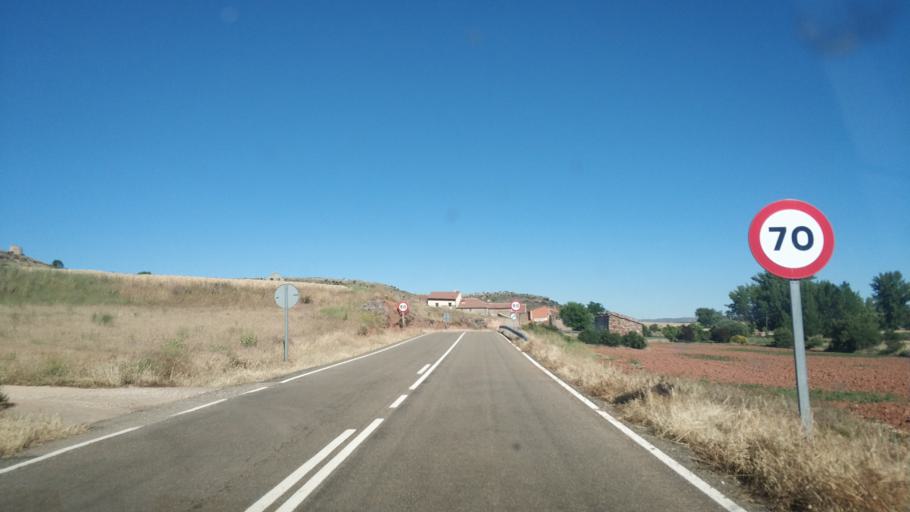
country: ES
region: Castille and Leon
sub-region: Provincia de Soria
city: Montejo de Tiermes
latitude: 41.3626
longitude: -3.1856
